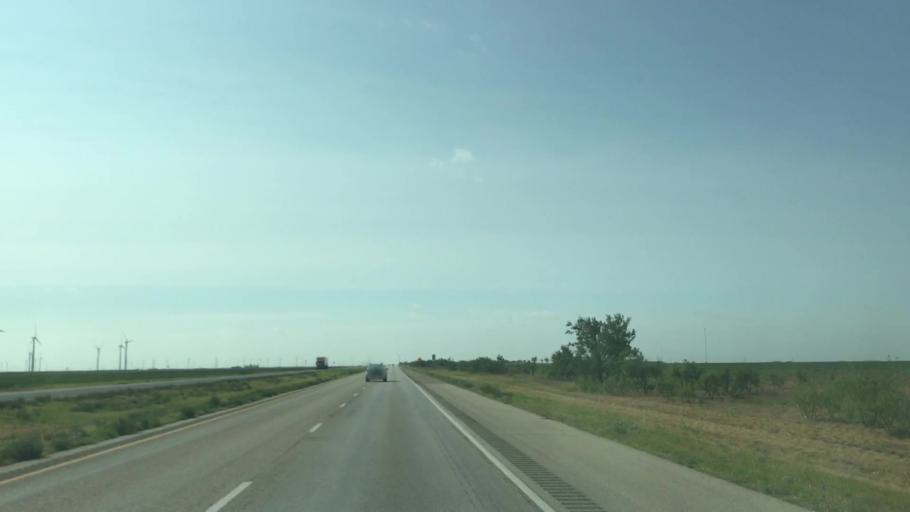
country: US
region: Texas
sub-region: Scurry County
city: Snyder
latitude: 32.6303
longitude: -100.7613
